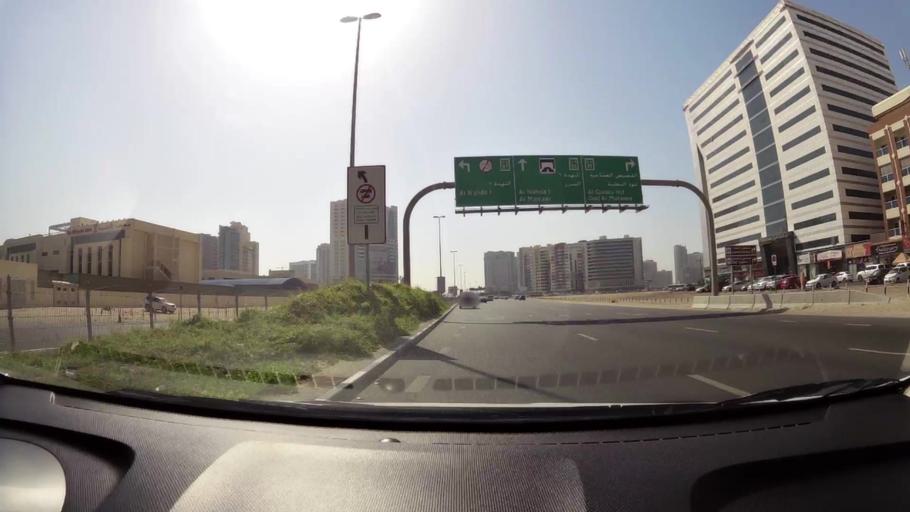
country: AE
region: Ash Shariqah
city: Sharjah
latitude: 25.2866
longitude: 55.3694
